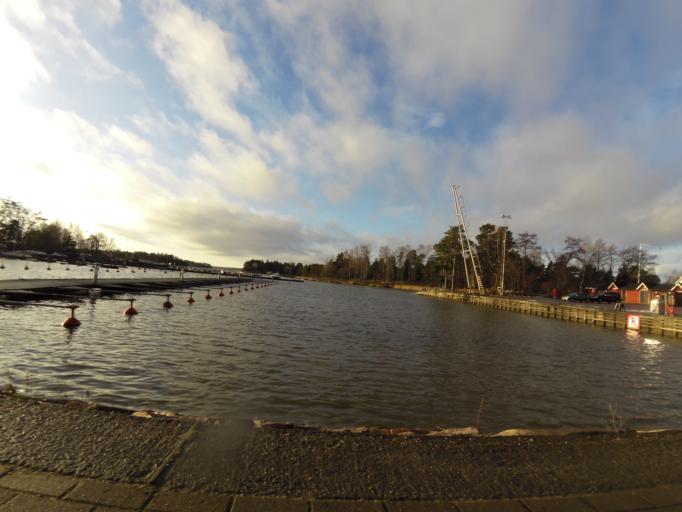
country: FI
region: Uusimaa
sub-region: Helsinki
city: Koukkuniemi
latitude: 60.1555
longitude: 24.7727
